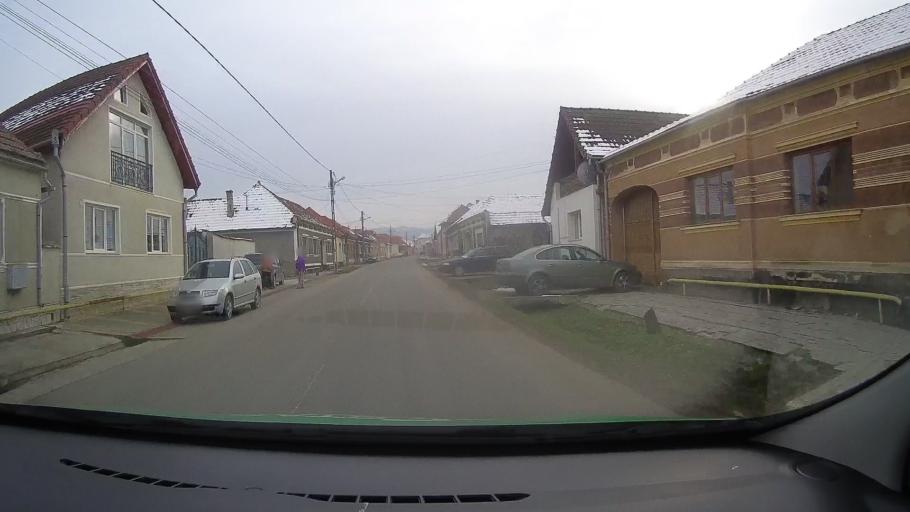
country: RO
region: Hunedoara
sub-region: Comuna Romos
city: Romos
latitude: 45.8452
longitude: 23.2735
